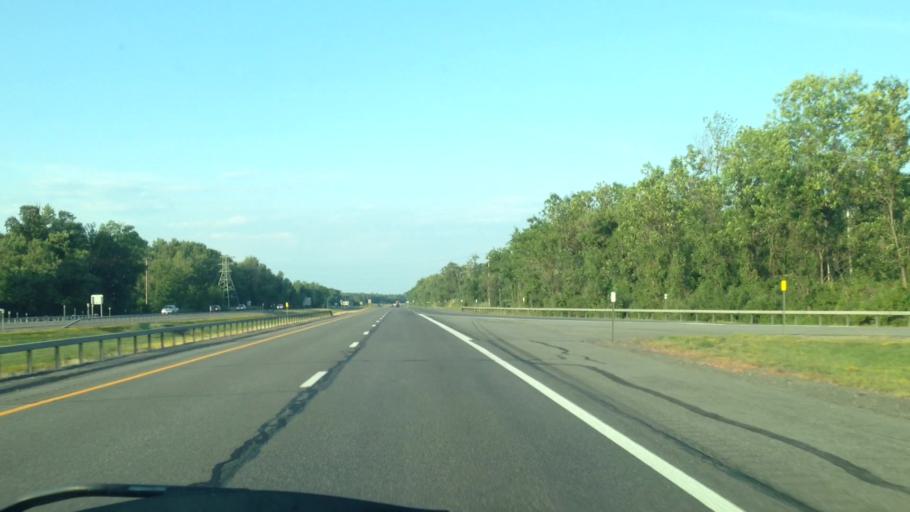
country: US
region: New York
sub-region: Madison County
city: Canastota
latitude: 43.0930
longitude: -75.7446
